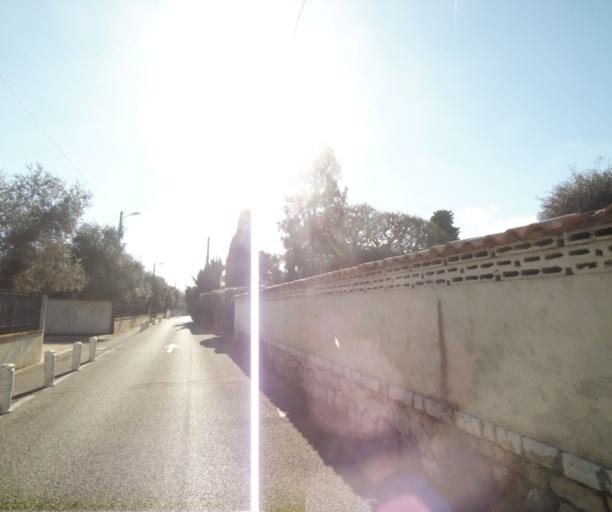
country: FR
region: Provence-Alpes-Cote d'Azur
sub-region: Departement des Alpes-Maritimes
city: Biot
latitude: 43.6188
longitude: 7.1240
